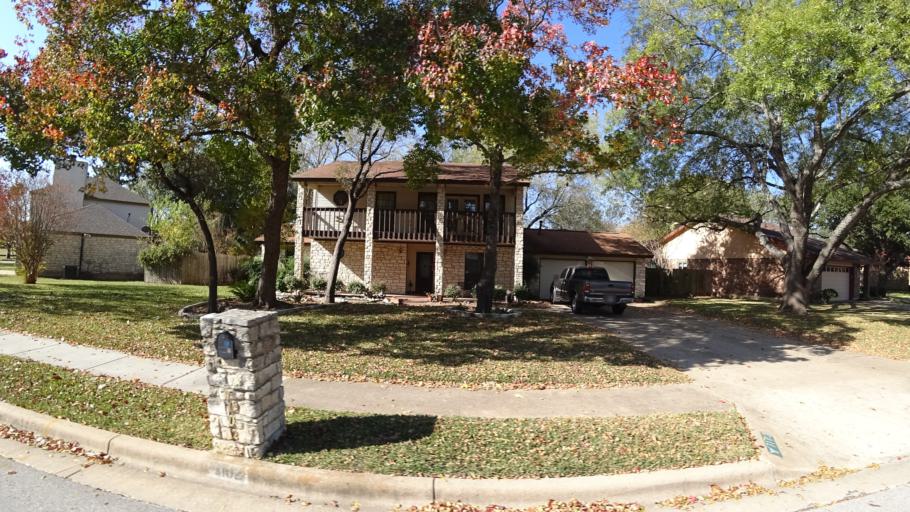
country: US
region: Texas
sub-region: Travis County
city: Shady Hollow
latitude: 30.2230
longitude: -97.8537
